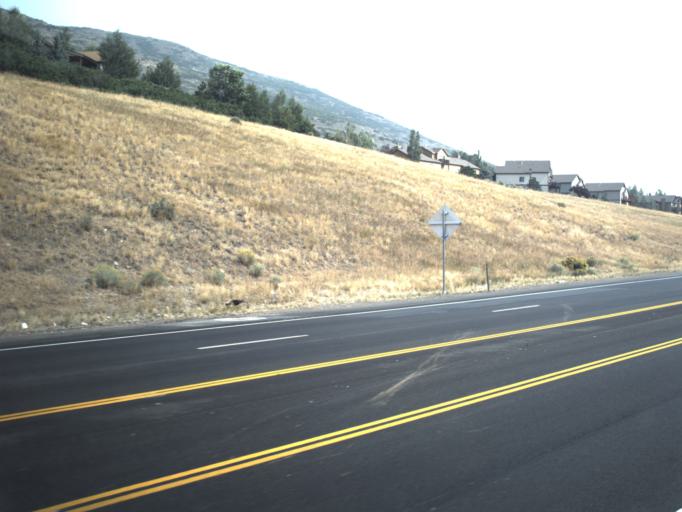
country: US
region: Utah
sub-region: Summit County
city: Park City
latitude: 40.6590
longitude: -111.4146
